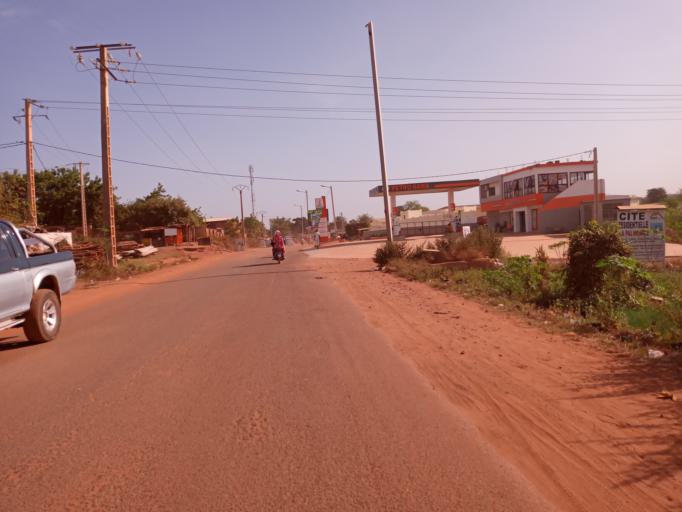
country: ML
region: Bamako
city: Bamako
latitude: 12.6242
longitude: -7.9551
